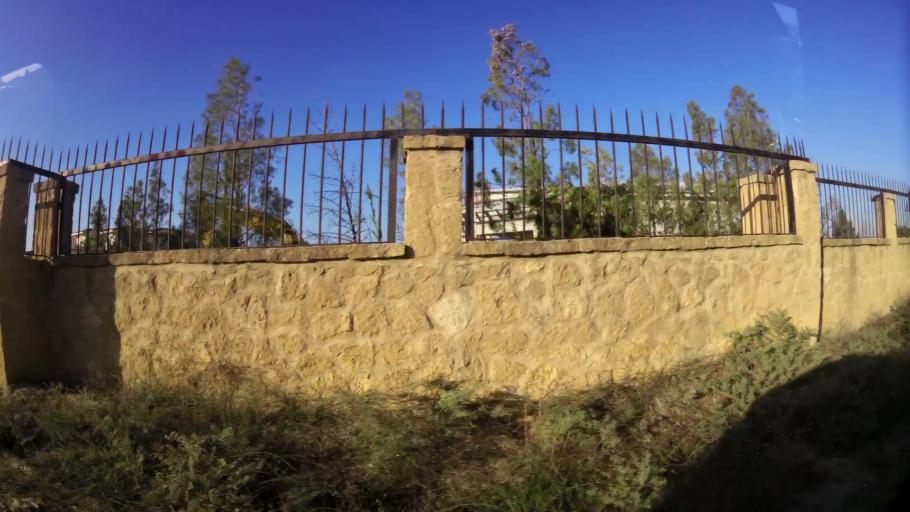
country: CY
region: Lefkosia
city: Nicosia
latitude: 35.2076
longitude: 33.2994
